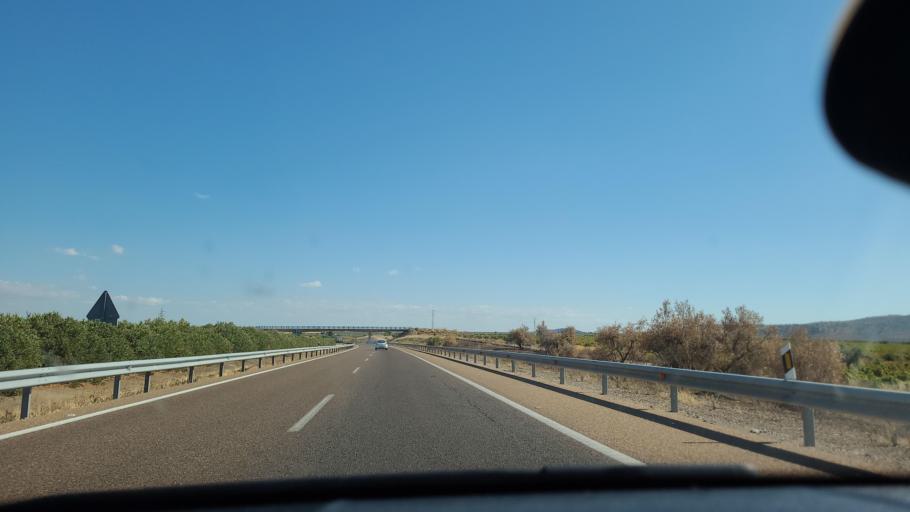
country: ES
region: Extremadura
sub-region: Provincia de Badajoz
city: Villafranca de los Barros
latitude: 38.5415
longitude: -6.3627
